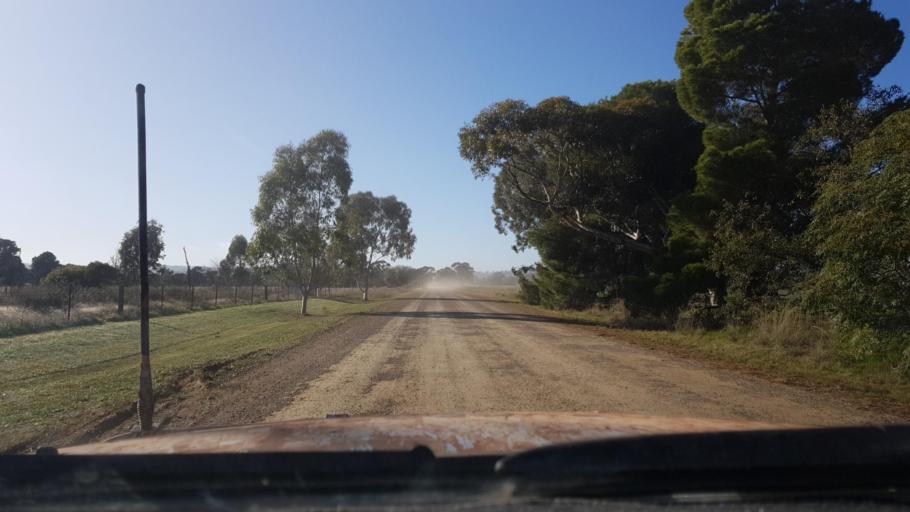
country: AU
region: New South Wales
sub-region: Wagga Wagga
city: Forest Hill
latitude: -35.0661
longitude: 147.4617
